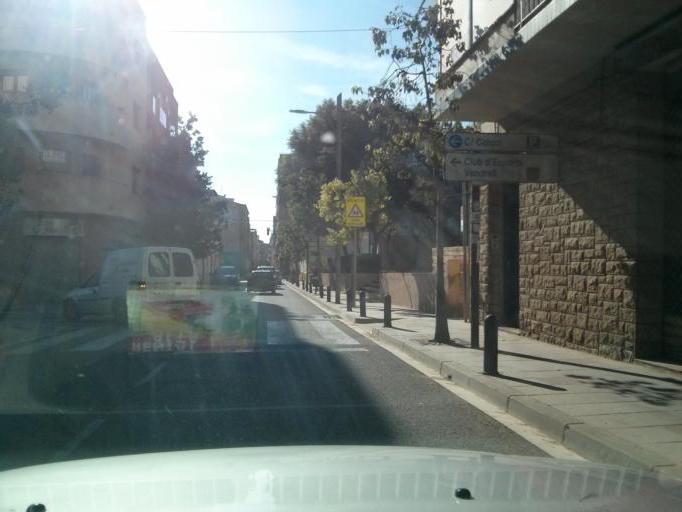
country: ES
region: Catalonia
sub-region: Provincia de Tarragona
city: El Vendrell
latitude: 41.2245
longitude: 1.5374
